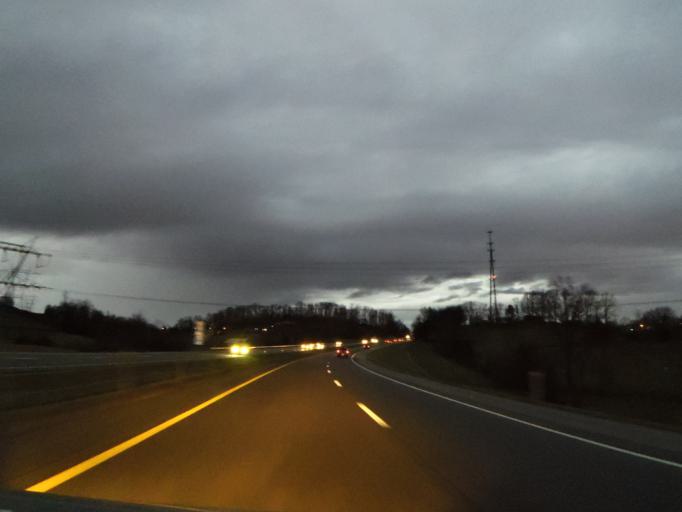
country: US
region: Tennessee
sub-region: Washington County
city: Gray
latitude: 36.4259
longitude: -82.5140
